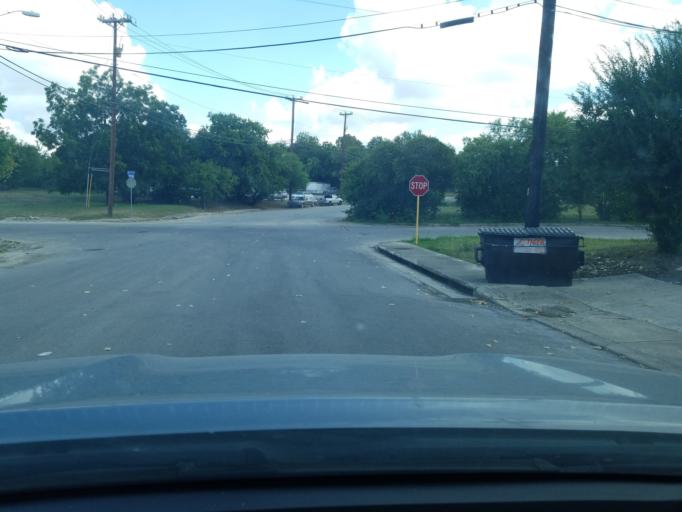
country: US
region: Texas
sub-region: Bexar County
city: Castle Hills
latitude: 29.5287
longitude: -98.4885
